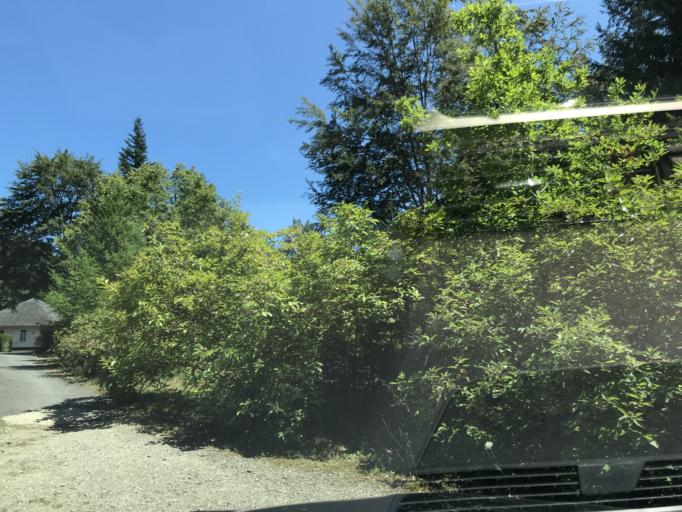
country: FR
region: Limousin
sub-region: Departement de la Correze
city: Neuvic
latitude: 45.3796
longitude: 2.2265
